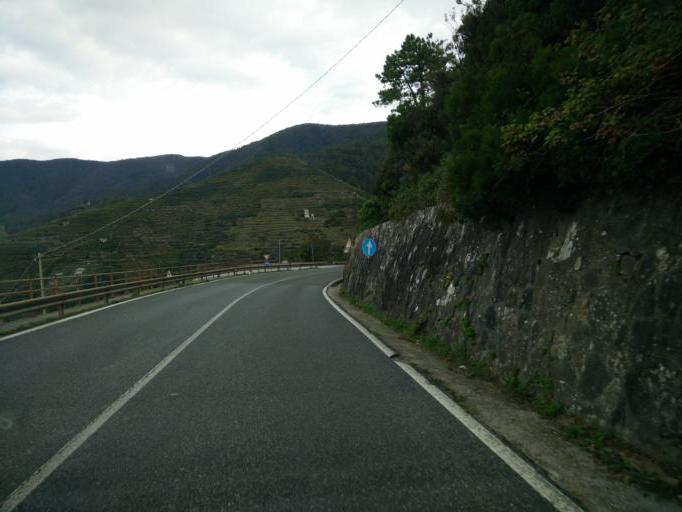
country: IT
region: Liguria
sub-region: Provincia di La Spezia
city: Riomaggiore
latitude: 44.0973
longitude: 9.7431
